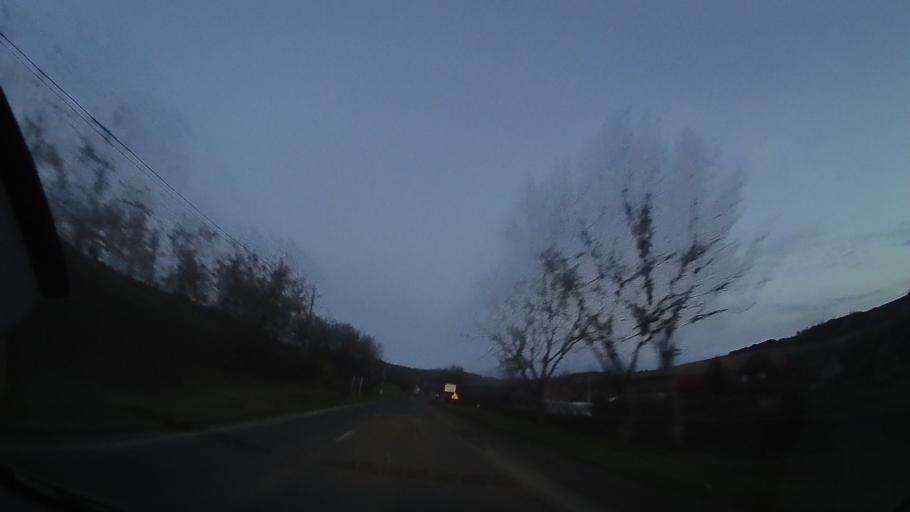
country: RO
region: Mures
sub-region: Comuna Sarmasu
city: Sarmasu
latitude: 46.7898
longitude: 24.1943
